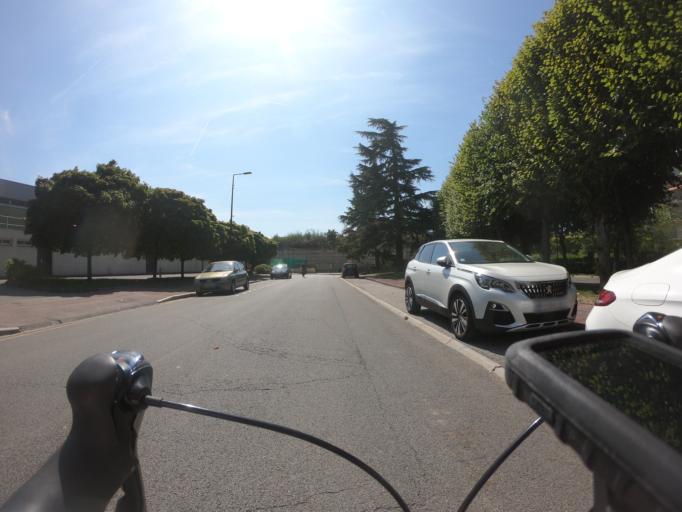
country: FR
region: Ile-de-France
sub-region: Departement des Yvelines
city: Viroflay
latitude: 48.7823
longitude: 2.1690
